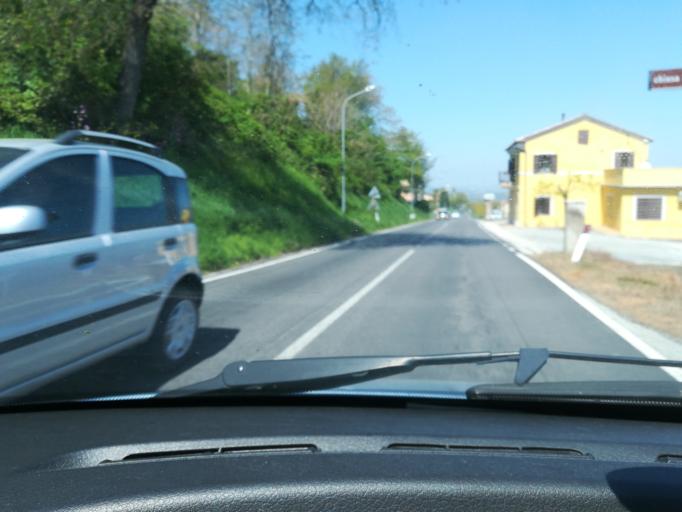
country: IT
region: The Marches
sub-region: Provincia di Macerata
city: Cingoli
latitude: 43.3747
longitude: 13.2190
